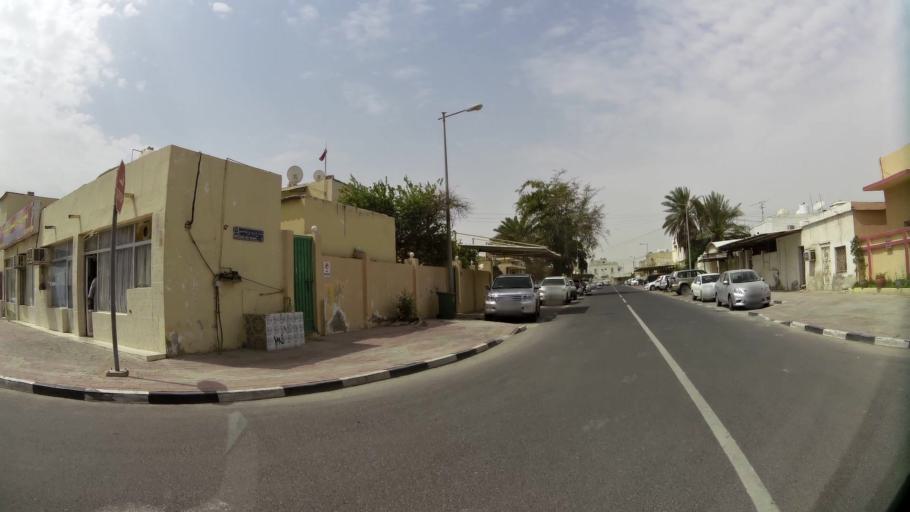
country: QA
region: Baladiyat ad Dawhah
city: Doha
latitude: 25.3136
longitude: 51.4865
